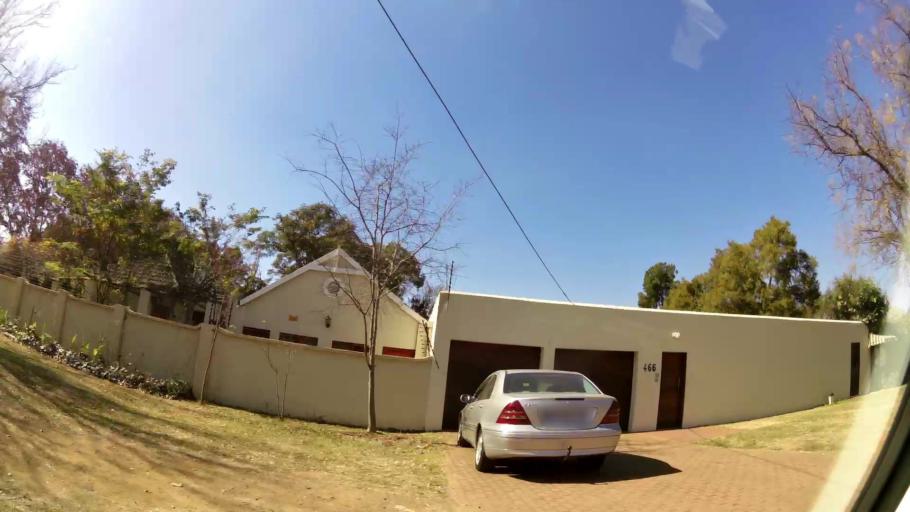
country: ZA
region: Gauteng
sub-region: City of Tshwane Metropolitan Municipality
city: Pretoria
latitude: -25.7504
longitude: 28.2450
